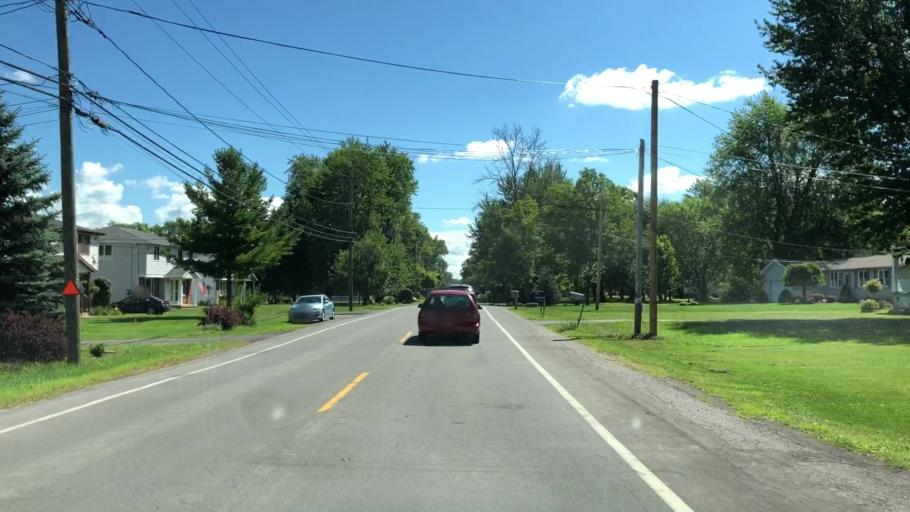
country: US
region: New York
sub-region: Erie County
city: Cheektowaga
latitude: 42.8509
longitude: -78.7343
